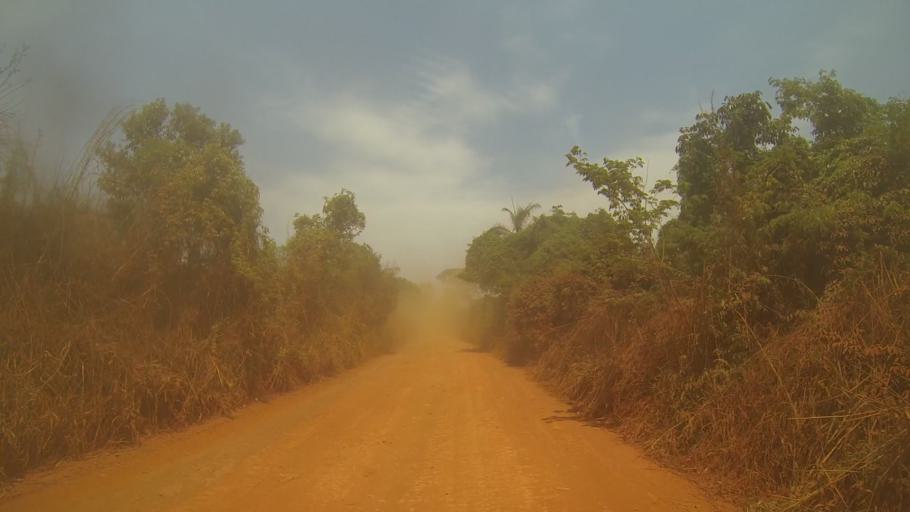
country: BR
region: Minas Gerais
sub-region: Bambui
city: Bambui
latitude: -20.0051
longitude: -45.9307
